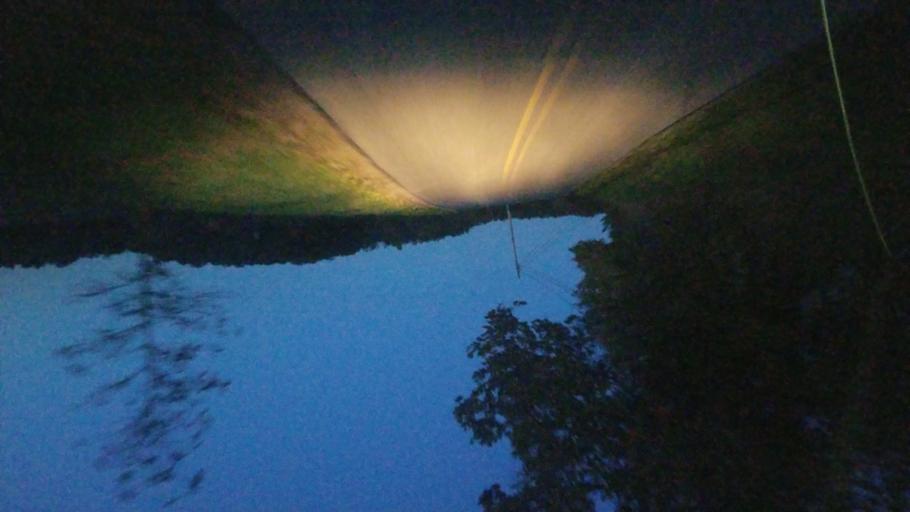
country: US
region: Ohio
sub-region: Perry County
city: Somerset
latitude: 39.8781
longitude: -82.2072
